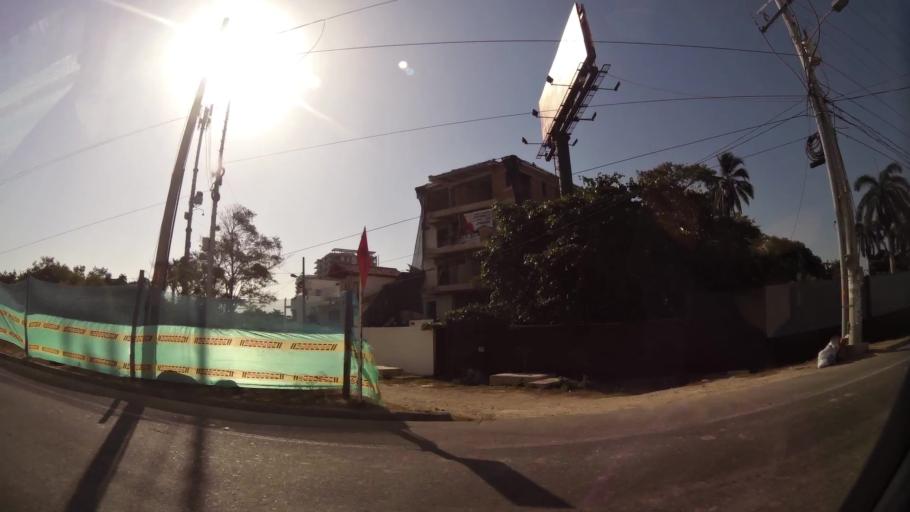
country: CO
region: Bolivar
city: Cartagena
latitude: 10.4588
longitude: -75.5071
